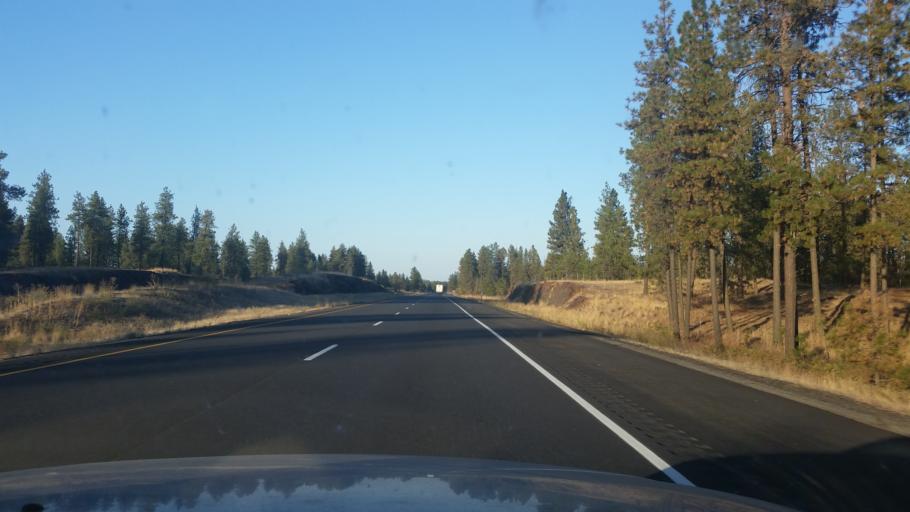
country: US
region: Washington
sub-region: Spokane County
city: Medical Lake
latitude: 47.5187
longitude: -117.6704
